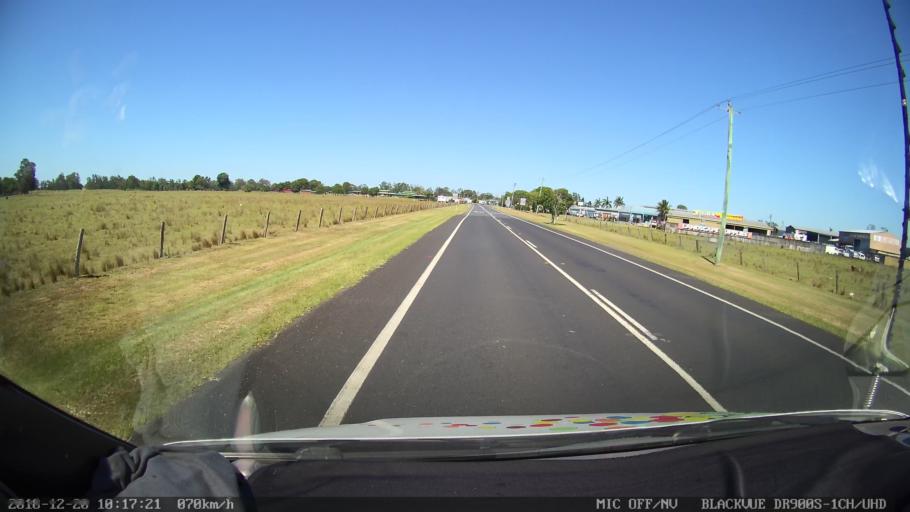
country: AU
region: New South Wales
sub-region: Richmond Valley
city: Casino
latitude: -28.8603
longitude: 153.0716
